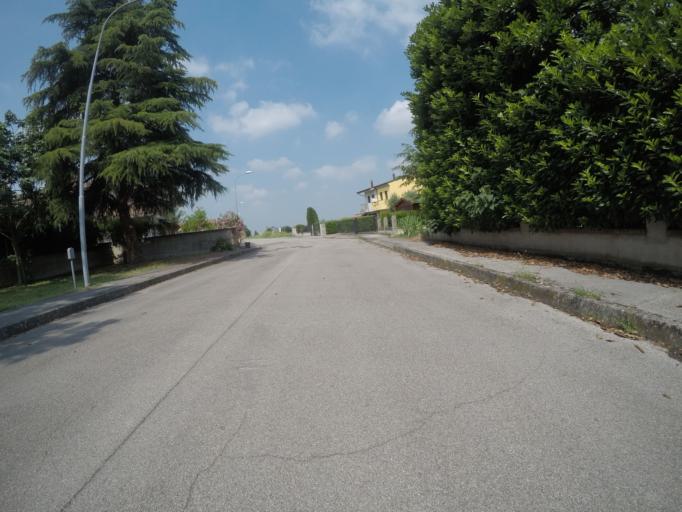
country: IT
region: Veneto
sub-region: Provincia di Rovigo
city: Villanova del Ghebbo Canton
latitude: 45.0574
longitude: 11.6407
